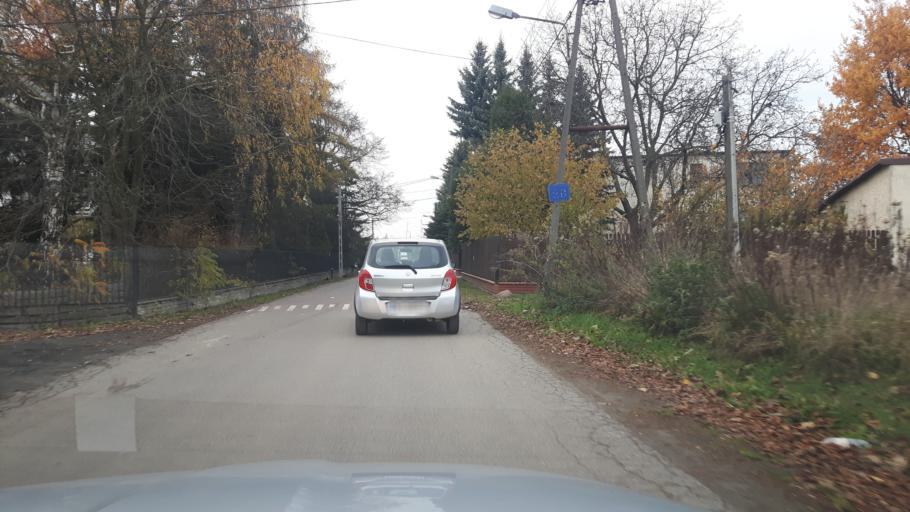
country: PL
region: Masovian Voivodeship
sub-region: Warszawa
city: Wilanow
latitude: 52.1615
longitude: 21.1249
